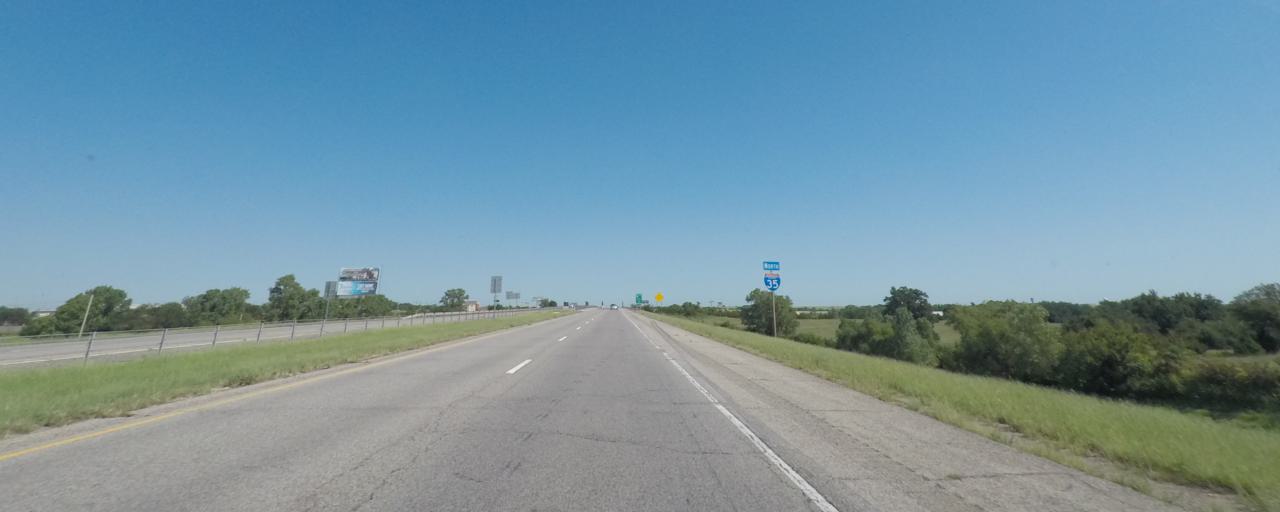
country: US
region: Oklahoma
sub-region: Noble County
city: Perry
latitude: 36.2816
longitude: -97.3276
